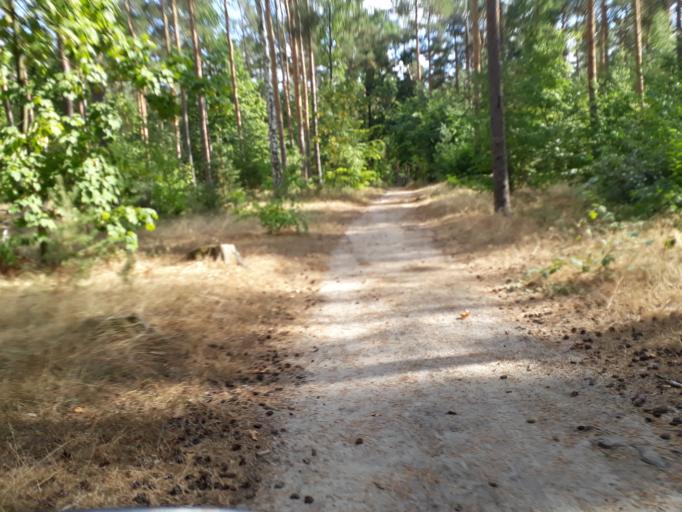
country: DE
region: Berlin
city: Grunewald
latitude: 52.4950
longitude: 13.2518
